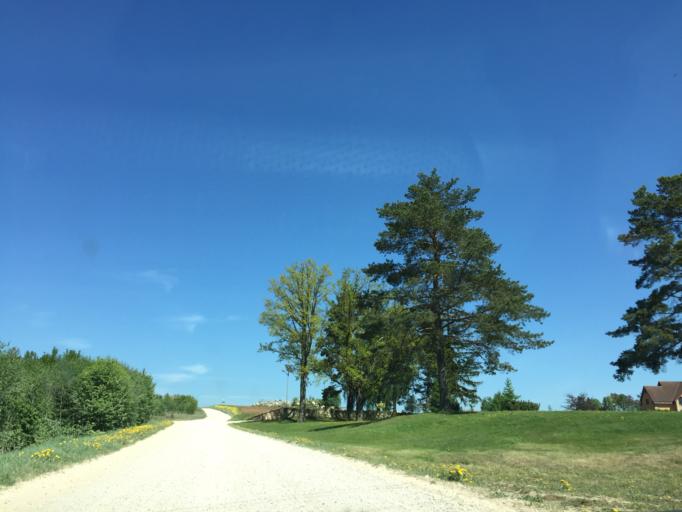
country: LV
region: Ikskile
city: Ikskile
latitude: 56.8634
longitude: 24.5018
